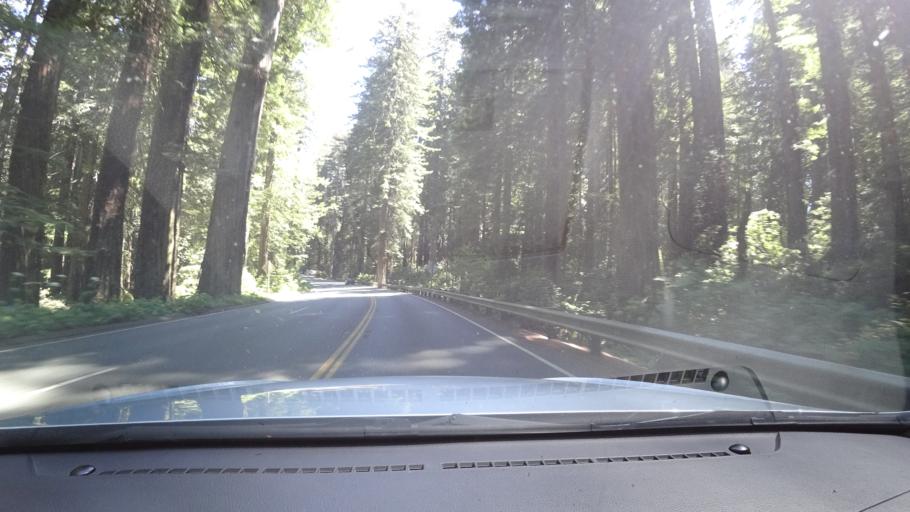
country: US
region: California
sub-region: Del Norte County
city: Bertsch-Oceanview
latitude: 41.6476
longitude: -124.1162
